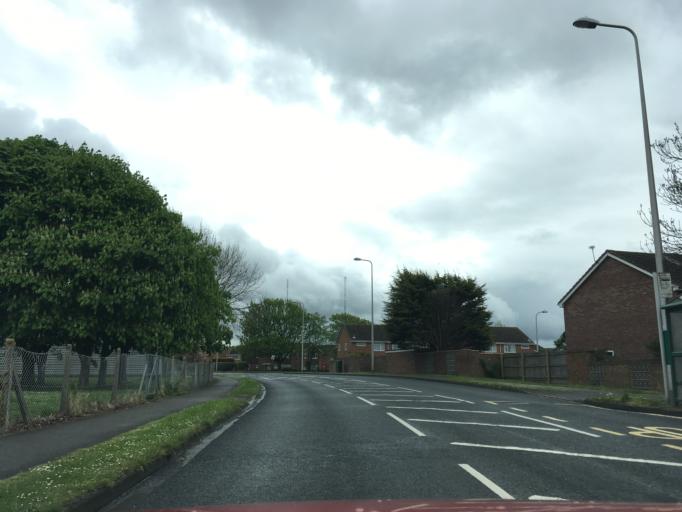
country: GB
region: England
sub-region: North Somerset
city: Clevedon
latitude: 51.4292
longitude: -2.8685
